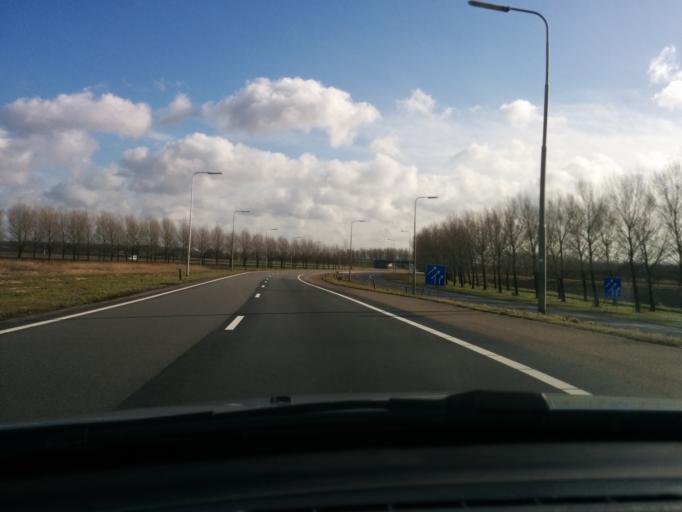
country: NL
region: Flevoland
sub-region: Gemeente Almere
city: Almere Stad
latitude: 52.3787
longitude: 5.3002
